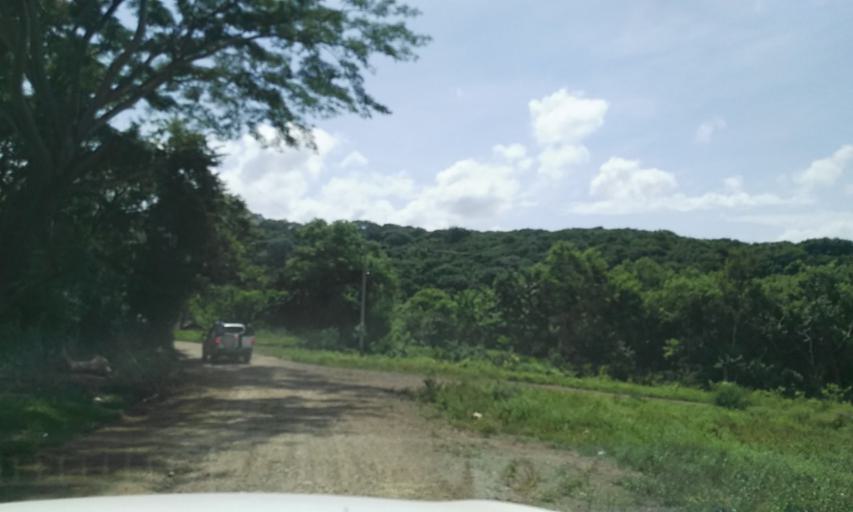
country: NI
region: Matagalpa
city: Terrabona
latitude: 12.6970
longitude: -85.9300
